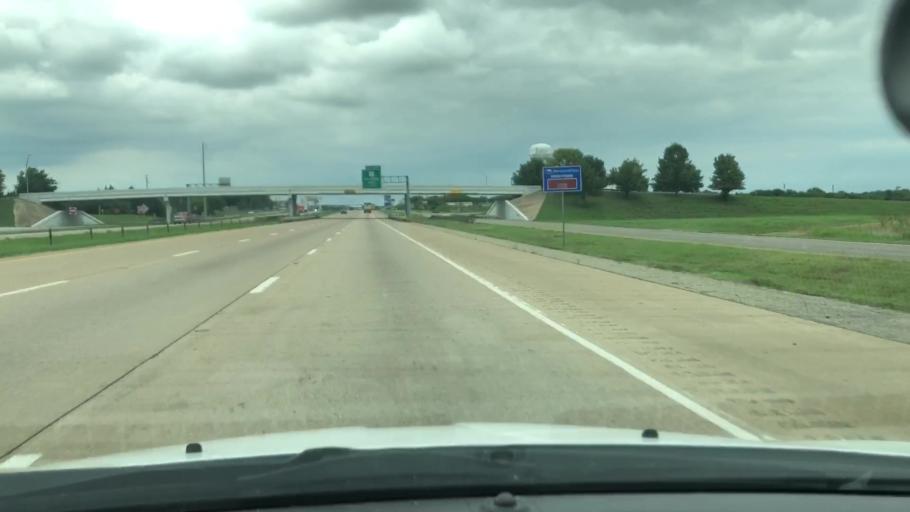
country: US
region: Texas
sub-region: Ellis County
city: Ennis
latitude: 32.3235
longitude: -96.6079
